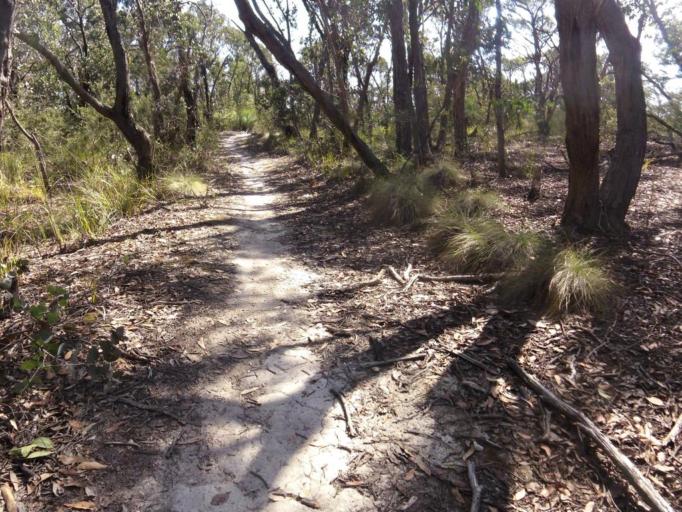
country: AU
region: Victoria
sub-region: Melton
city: Melton West
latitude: -37.5102
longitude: 144.5532
